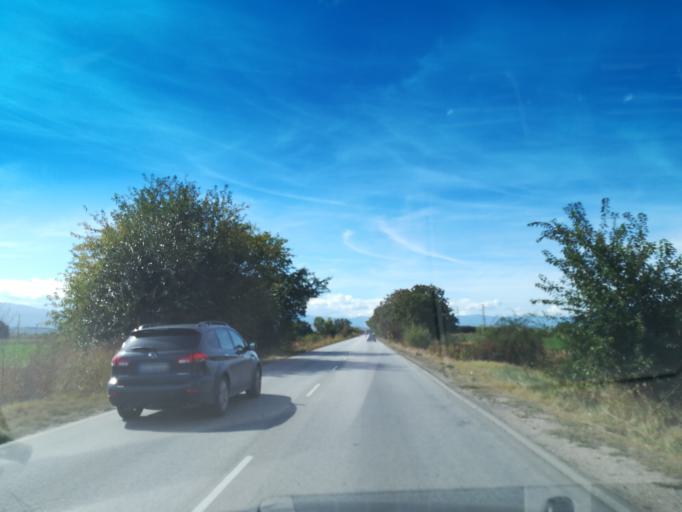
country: BG
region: Plovdiv
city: Stamboliyski
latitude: 42.1250
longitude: 24.5869
